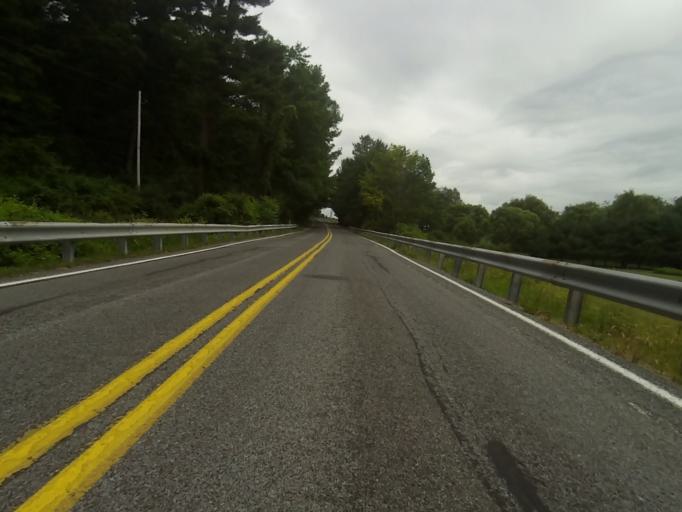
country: US
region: Pennsylvania
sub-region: Centre County
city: Stormstown
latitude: 40.7406
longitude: -77.9619
